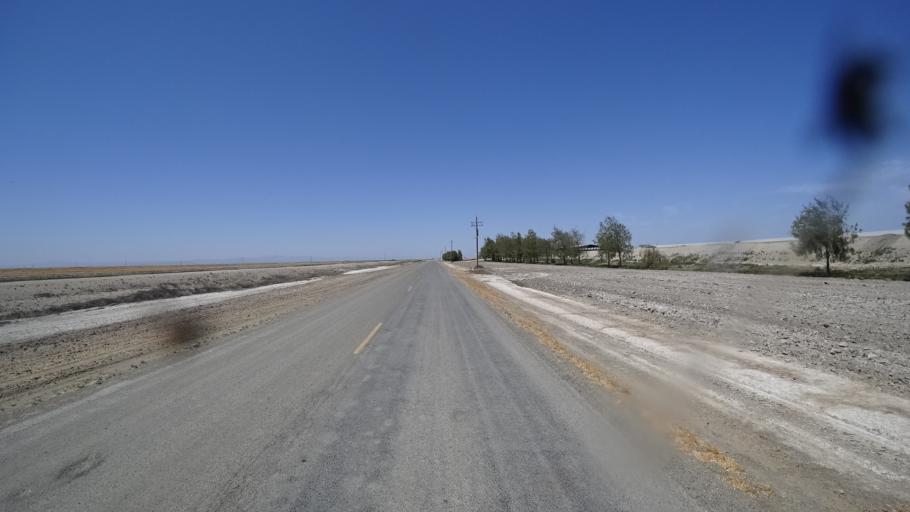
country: US
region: California
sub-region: Kings County
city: Stratford
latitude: 36.1526
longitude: -119.7387
